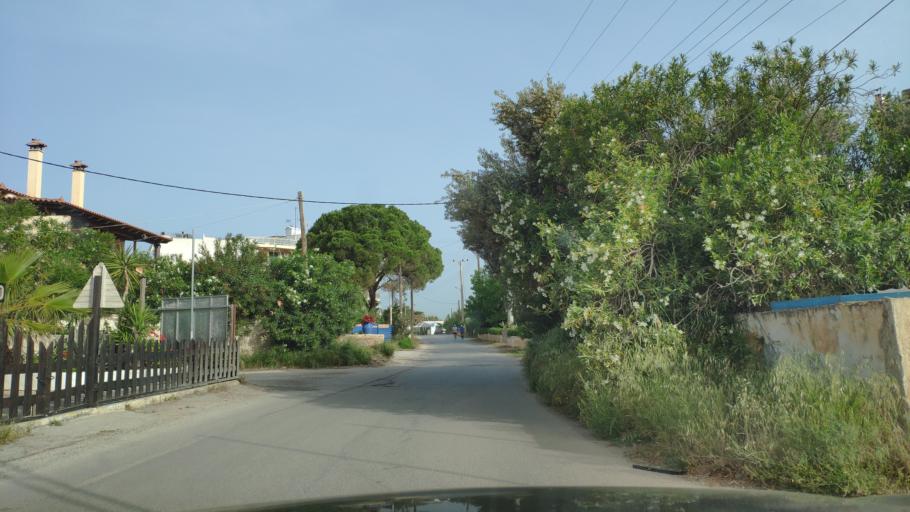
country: GR
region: Attica
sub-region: Nomarchia Anatolikis Attikis
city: Limin Mesoyaias
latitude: 37.8677
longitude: 24.0322
